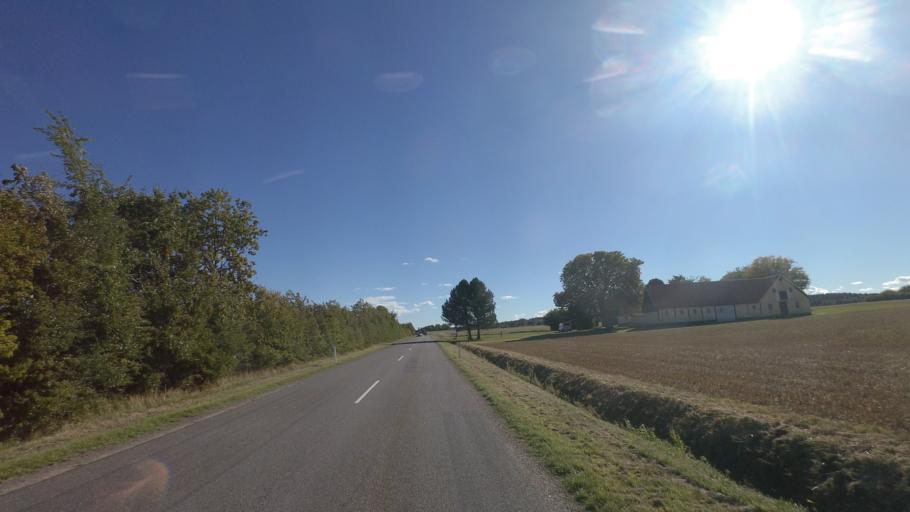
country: DK
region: Capital Region
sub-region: Bornholm Kommune
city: Nexo
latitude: 55.1121
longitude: 15.1099
